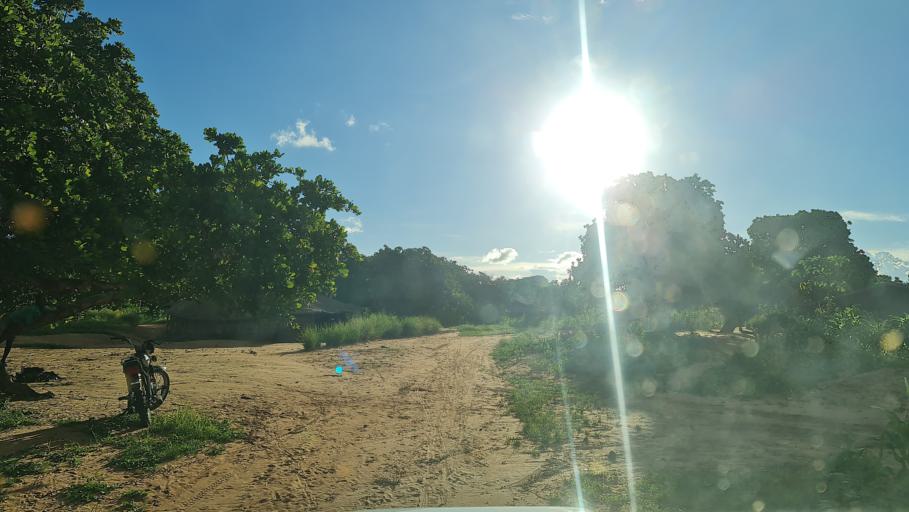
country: MZ
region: Nampula
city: Ilha de Mocambique
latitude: -14.9441
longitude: 40.1637
